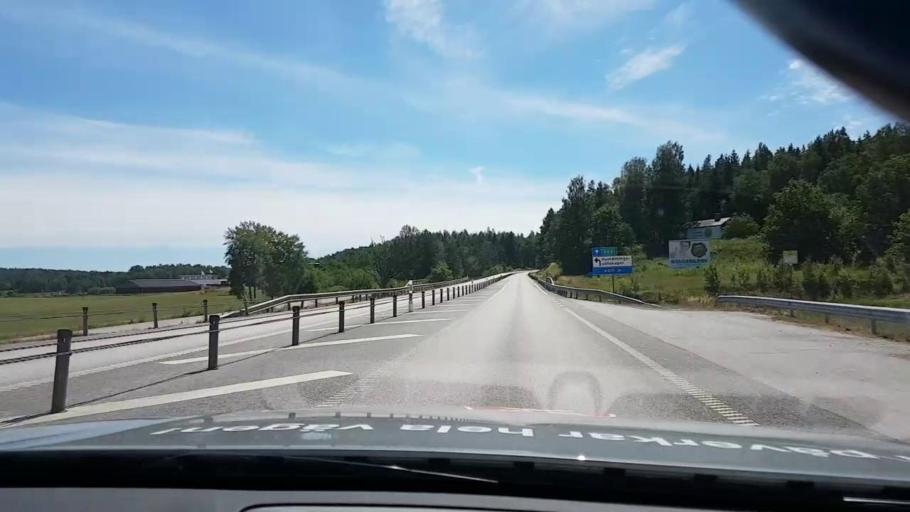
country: SE
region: Kalmar
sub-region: Vasterviks Kommun
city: Gamleby
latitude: 57.9201
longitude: 16.3995
